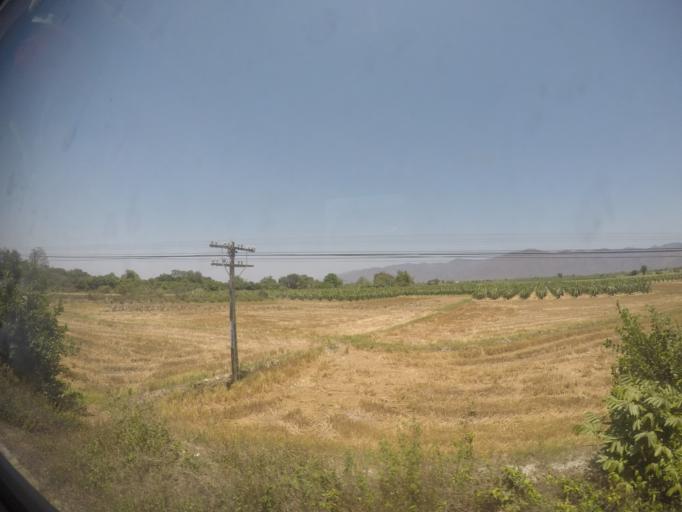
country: VN
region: Binh Thuan
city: Cho Lau
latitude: 11.2519
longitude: 108.5164
